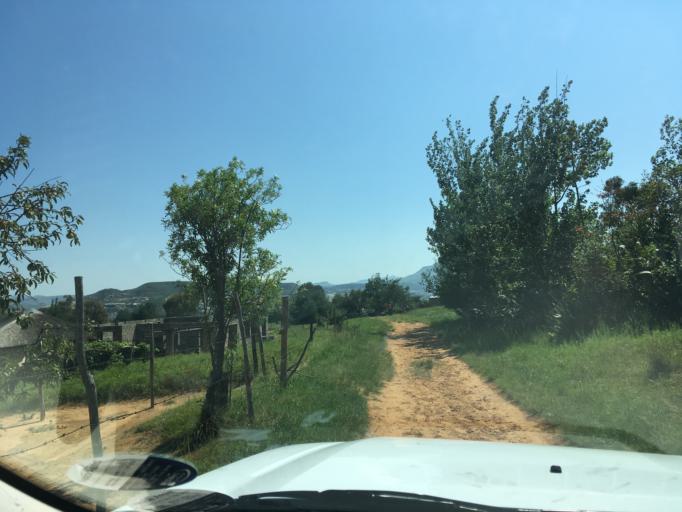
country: LS
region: Butha-Buthe
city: Butha-Buthe
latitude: -28.7257
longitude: 28.3653
